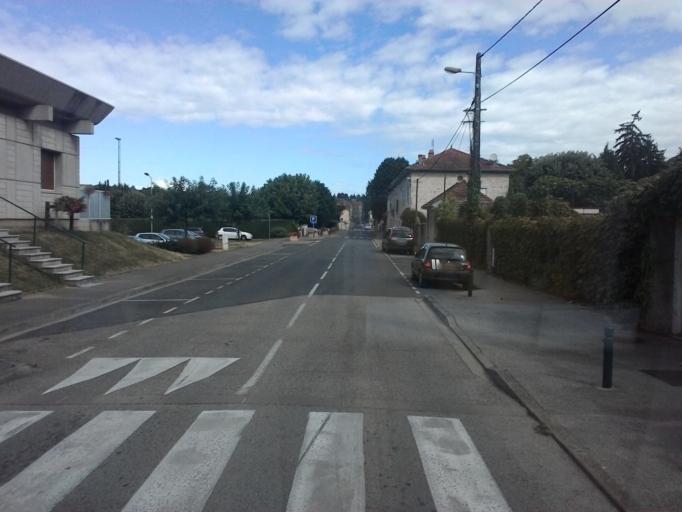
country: FR
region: Rhone-Alpes
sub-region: Departement de l'Ain
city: Lagnieu
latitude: 45.8997
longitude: 5.3524
